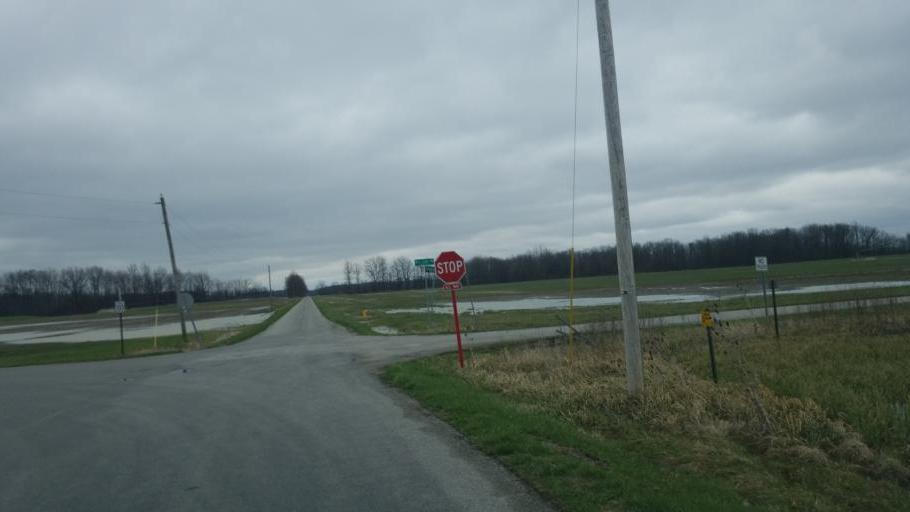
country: US
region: Ohio
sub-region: Wyandot County
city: Upper Sandusky
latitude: 40.6873
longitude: -83.3625
